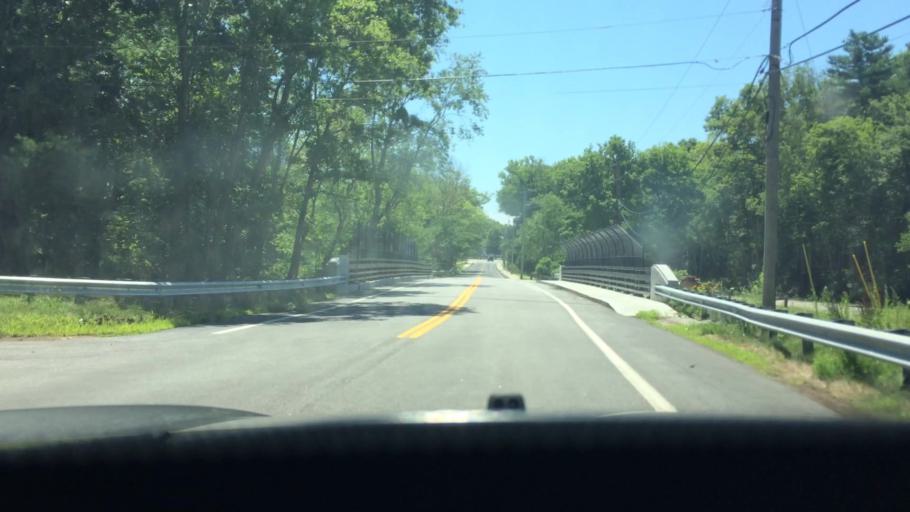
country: US
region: Rhode Island
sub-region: Providence County
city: Harrisville
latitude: 41.9714
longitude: -71.6785
